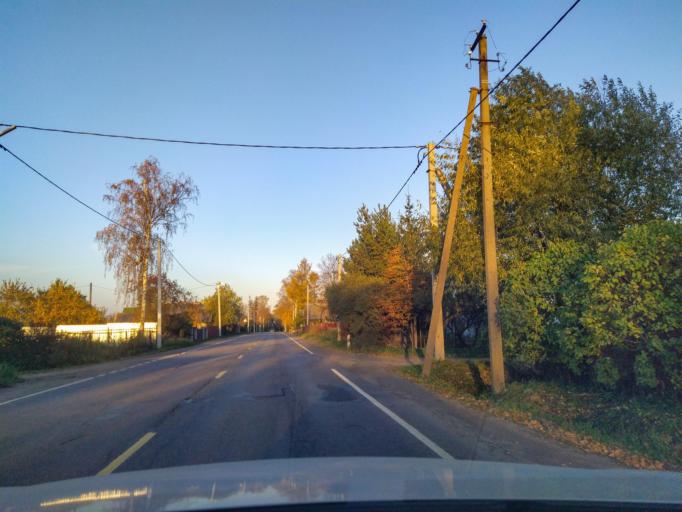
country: RU
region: Leningrad
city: Kobrinskoye
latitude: 59.4744
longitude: 30.1247
